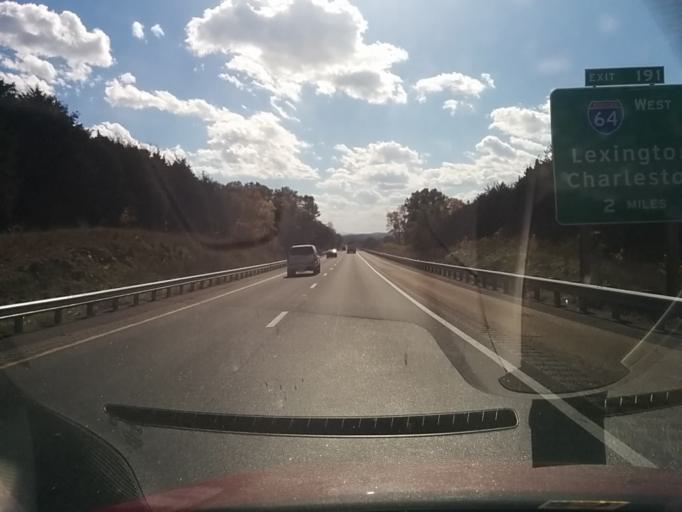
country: US
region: Virginia
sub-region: Rockbridge County
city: East Lexington
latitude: 37.8225
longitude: -79.3789
